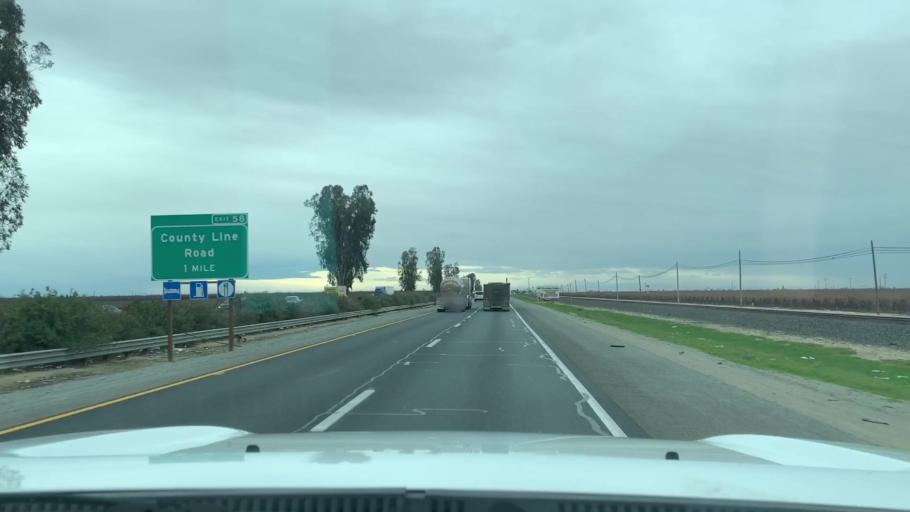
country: US
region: California
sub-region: Kern County
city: Delano
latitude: 35.8116
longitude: -119.2576
